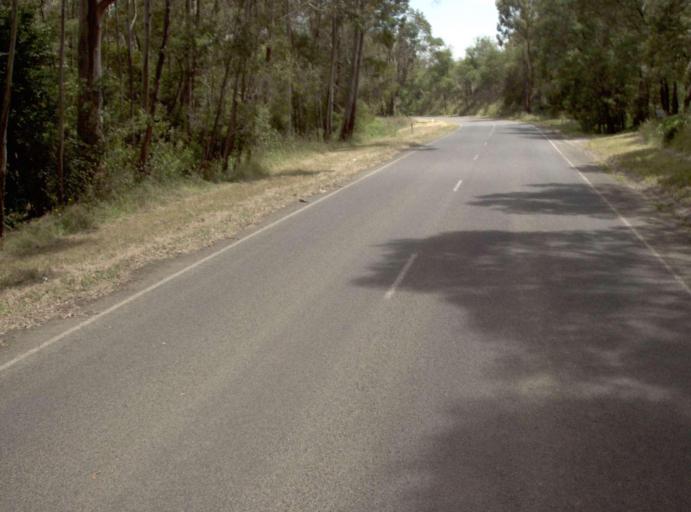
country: AU
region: Victoria
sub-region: Baw Baw
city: Warragul
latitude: -38.5073
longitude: 146.0052
